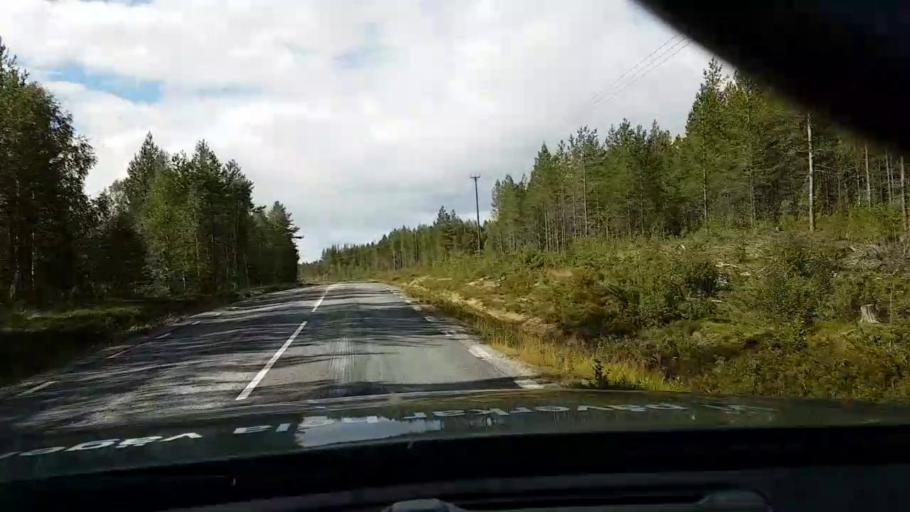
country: SE
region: Vaesterbotten
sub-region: Asele Kommun
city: Asele
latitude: 63.8472
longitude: 17.4126
